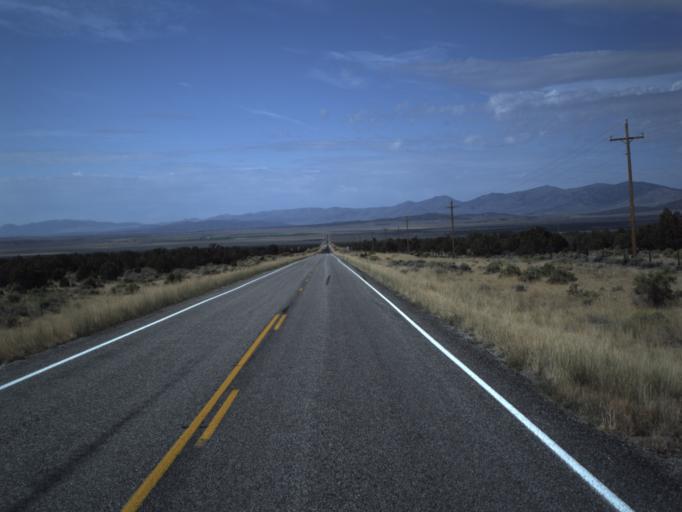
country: US
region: Idaho
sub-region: Cassia County
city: Burley
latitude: 41.8182
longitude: -113.4316
